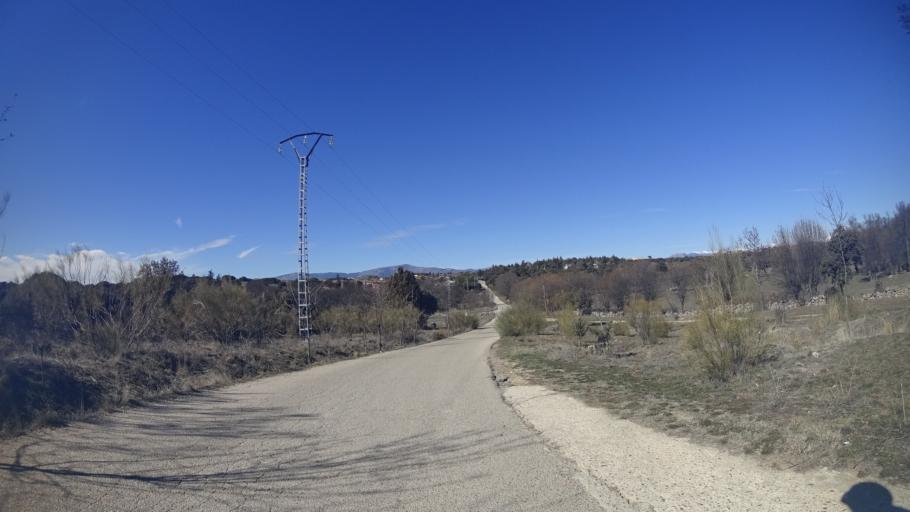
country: ES
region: Madrid
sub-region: Provincia de Madrid
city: Colmenarejo
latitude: 40.5476
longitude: -3.9989
